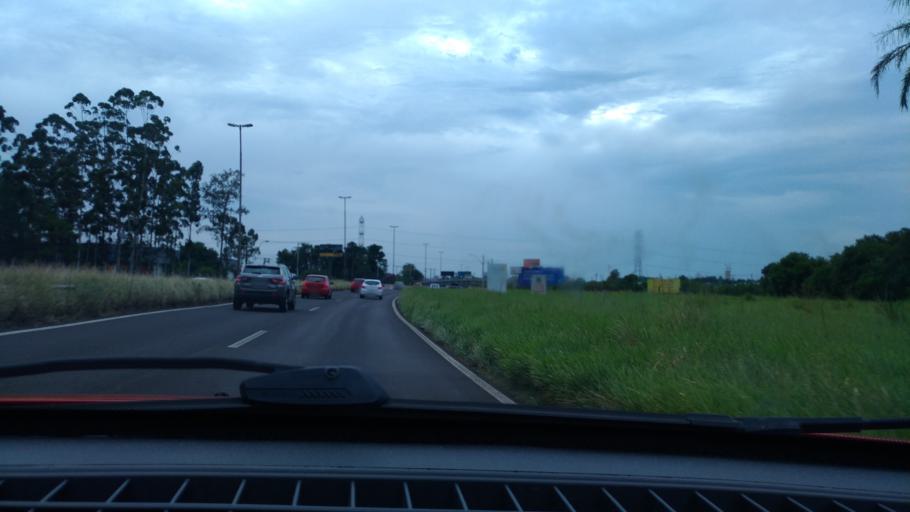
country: BR
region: Rio Grande do Sul
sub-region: Esteio
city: Esteio
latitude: -29.8729
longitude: -51.1796
